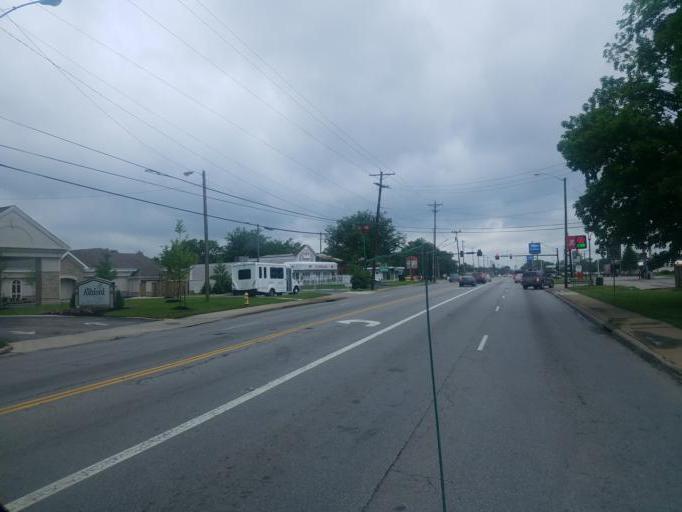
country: US
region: Ohio
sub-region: Franklin County
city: Whitehall
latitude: 39.9764
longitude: -82.8725
